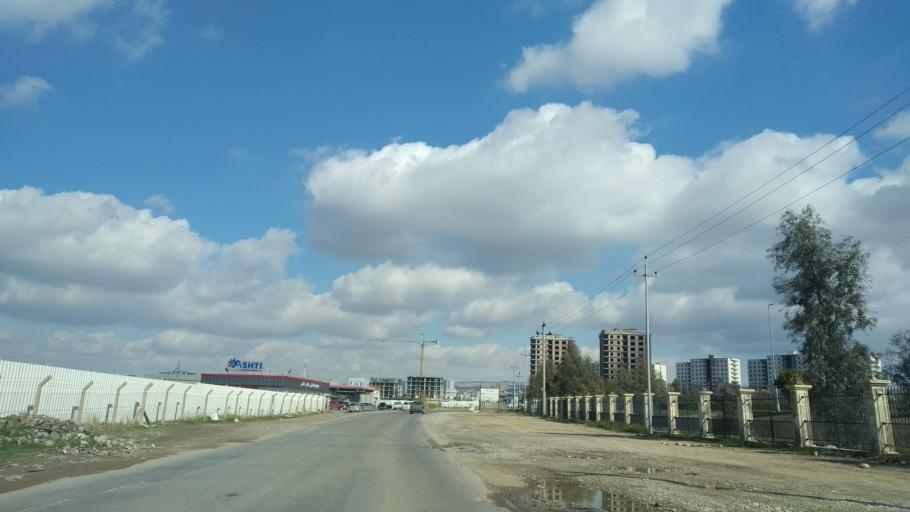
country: IQ
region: Arbil
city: Erbil
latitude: 36.2113
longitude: 44.1350
